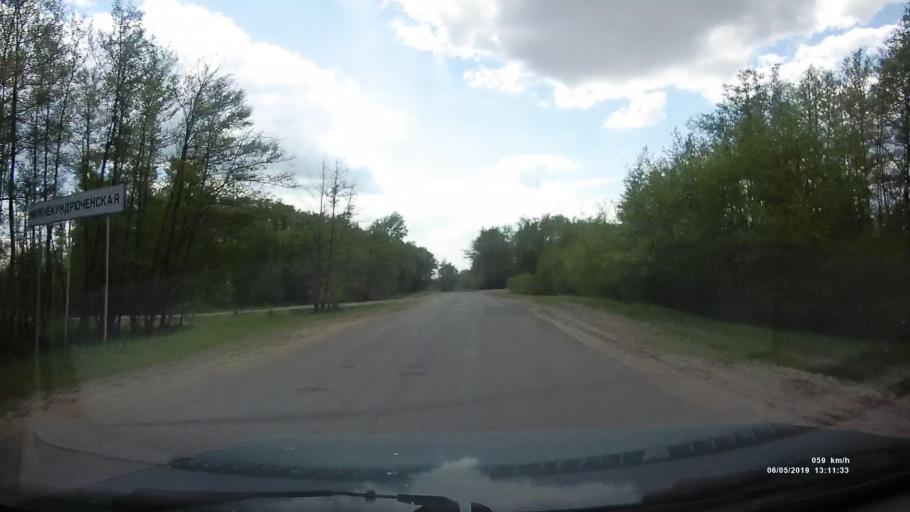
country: RU
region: Rostov
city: Ust'-Donetskiy
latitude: 47.7546
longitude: 40.9573
